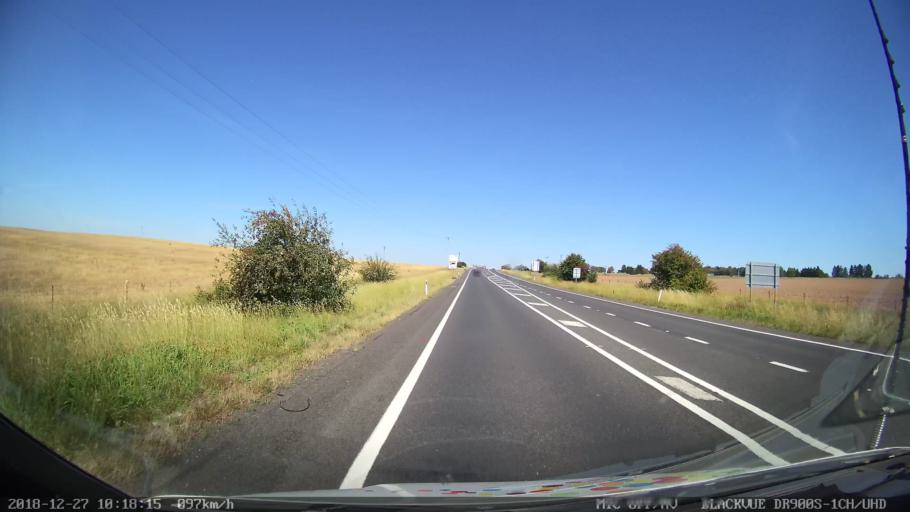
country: AU
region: New South Wales
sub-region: Bathurst Regional
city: Kelso
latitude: -33.4242
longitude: 149.6643
